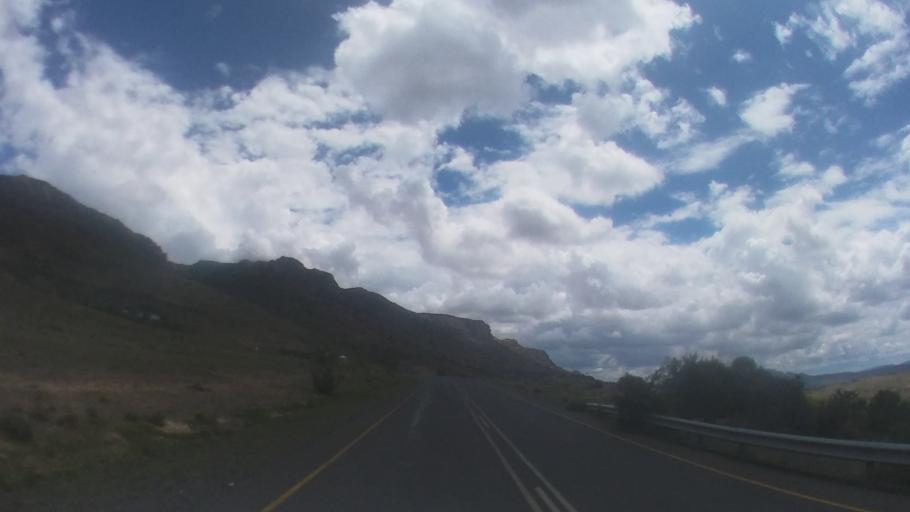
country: LS
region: Maseru
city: Maseru
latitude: -29.4445
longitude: 27.4740
